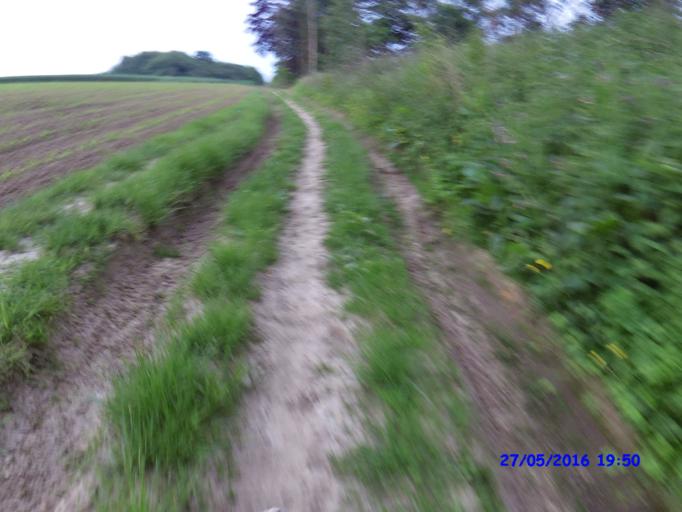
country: BE
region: Flanders
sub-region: Provincie Vlaams-Brabant
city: Asse
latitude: 50.9209
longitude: 4.1453
